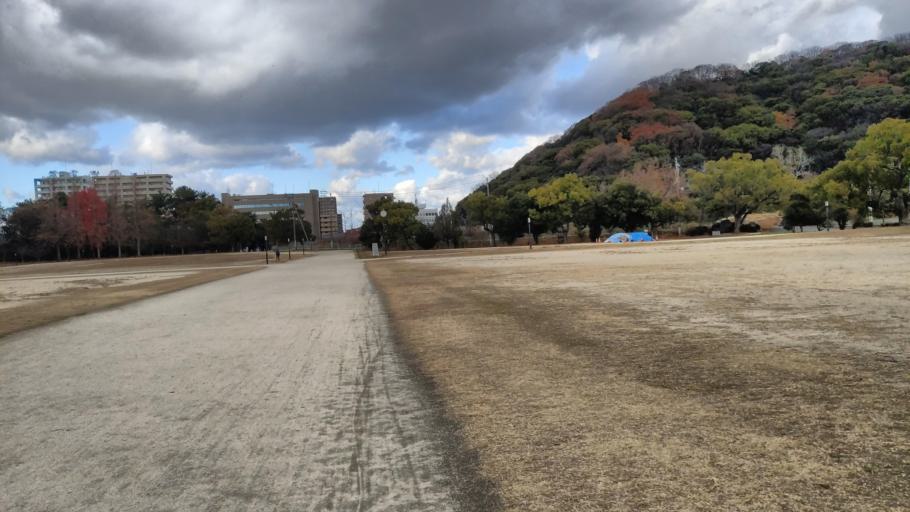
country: JP
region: Ehime
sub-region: Shikoku-chuo Shi
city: Matsuyama
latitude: 33.8418
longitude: 132.7607
